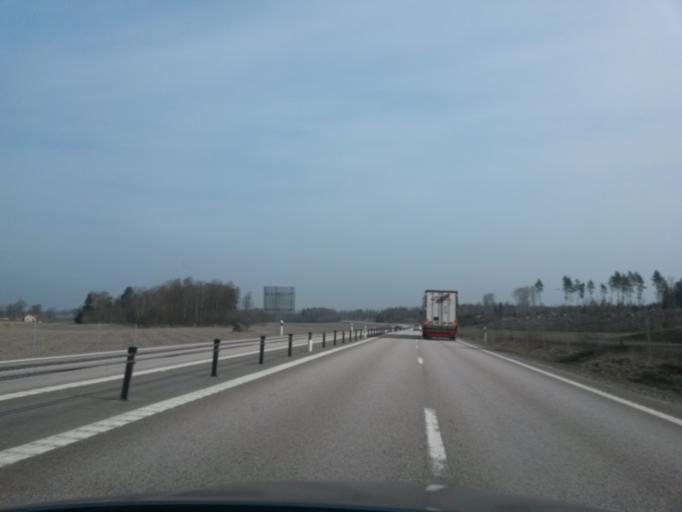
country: SE
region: Vaestra Goetaland
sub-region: Mariestads Kommun
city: Mariestad
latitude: 58.7542
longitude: 13.9618
